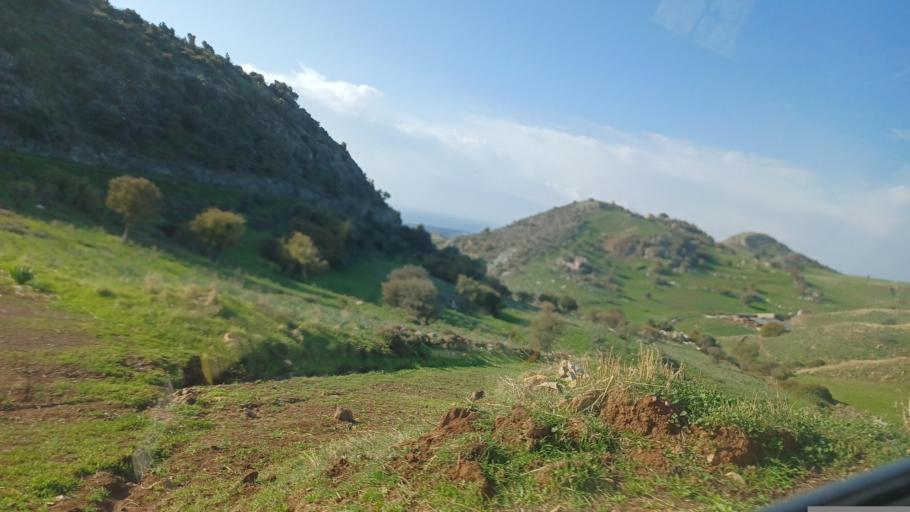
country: CY
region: Pafos
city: Mesogi
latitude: 34.7725
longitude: 32.5467
